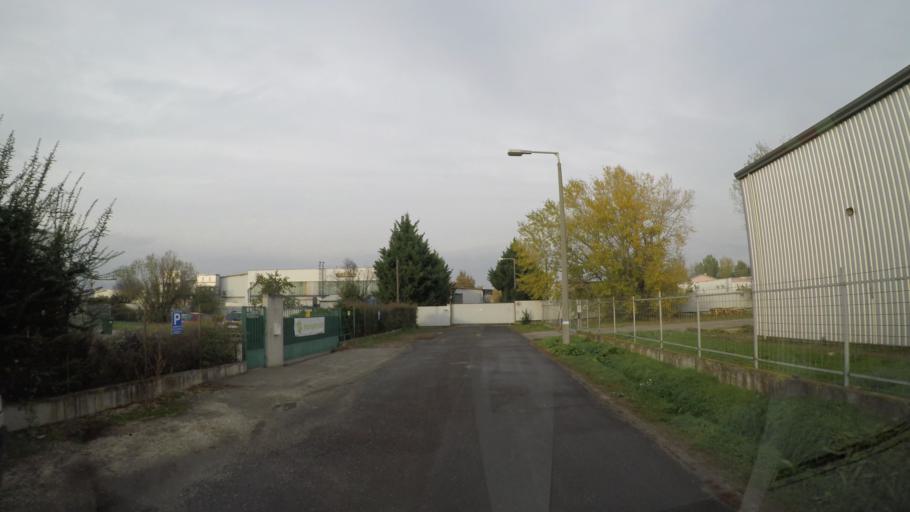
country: HU
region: Pest
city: Szentendre
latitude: 47.6586
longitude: 19.0636
